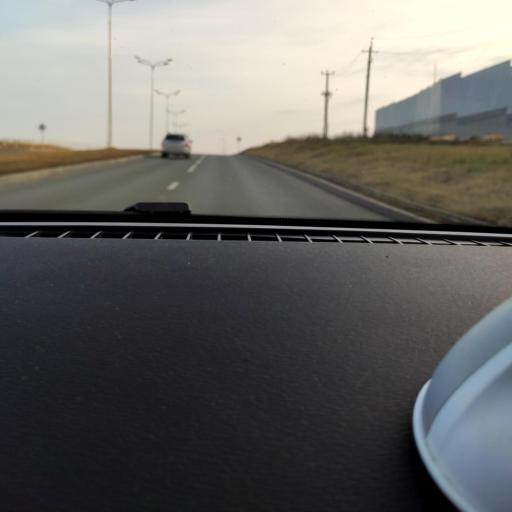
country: RU
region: Samara
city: Samara
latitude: 53.2845
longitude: 50.2368
